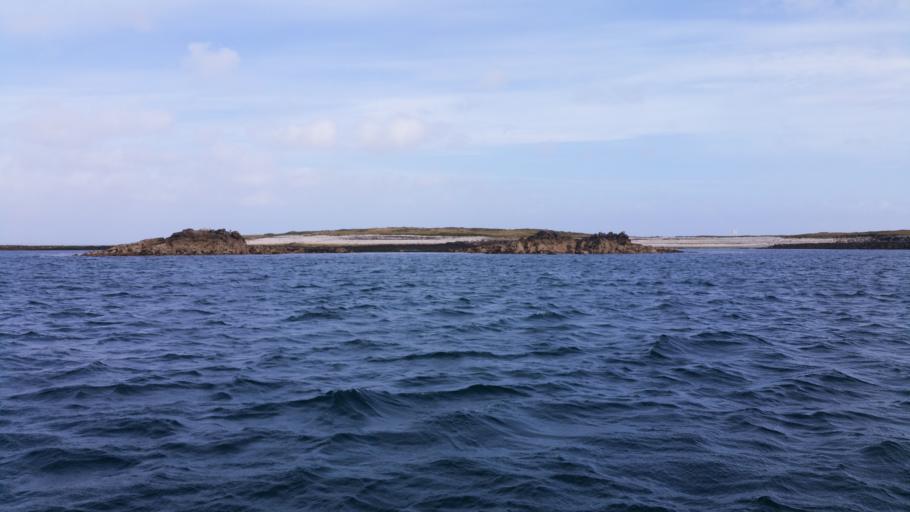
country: FR
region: Brittany
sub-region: Departement du Finistere
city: Le Conquet
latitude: 48.4047
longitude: -4.9538
